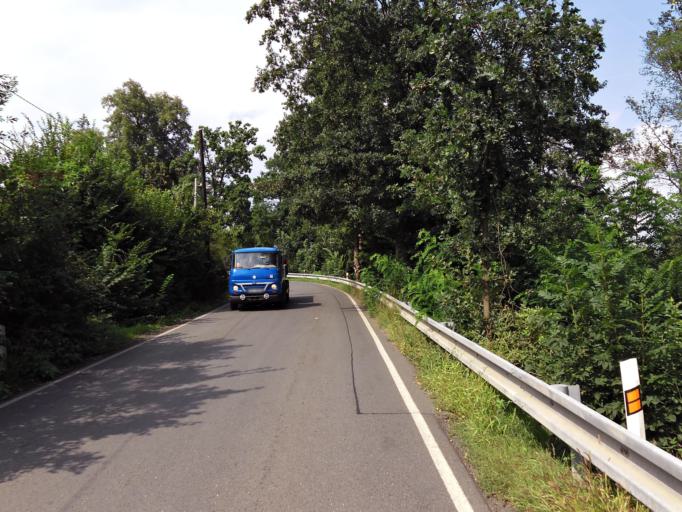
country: CZ
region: Central Bohemia
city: Kamenny Privoz
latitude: 49.8639
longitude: 14.4989
